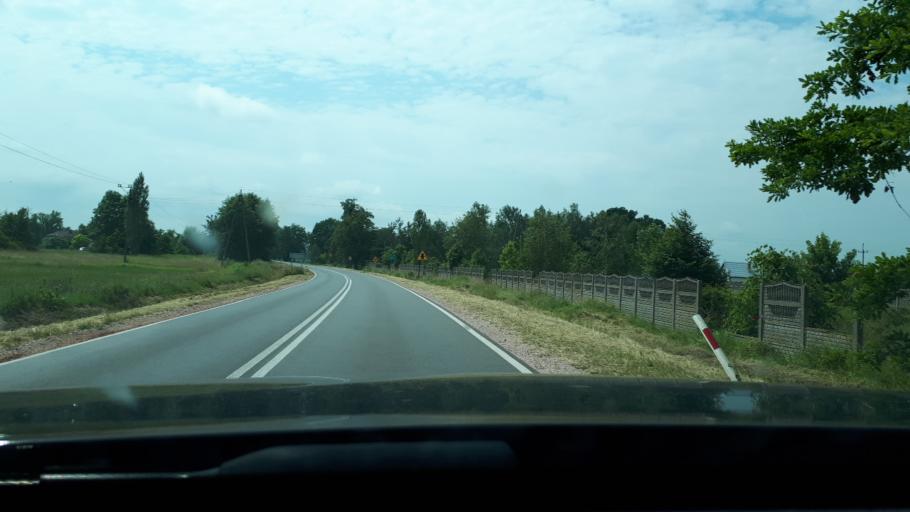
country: PL
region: Masovian Voivodeship
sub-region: Powiat warszawski zachodni
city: Kampinos
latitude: 52.2701
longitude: 20.4008
